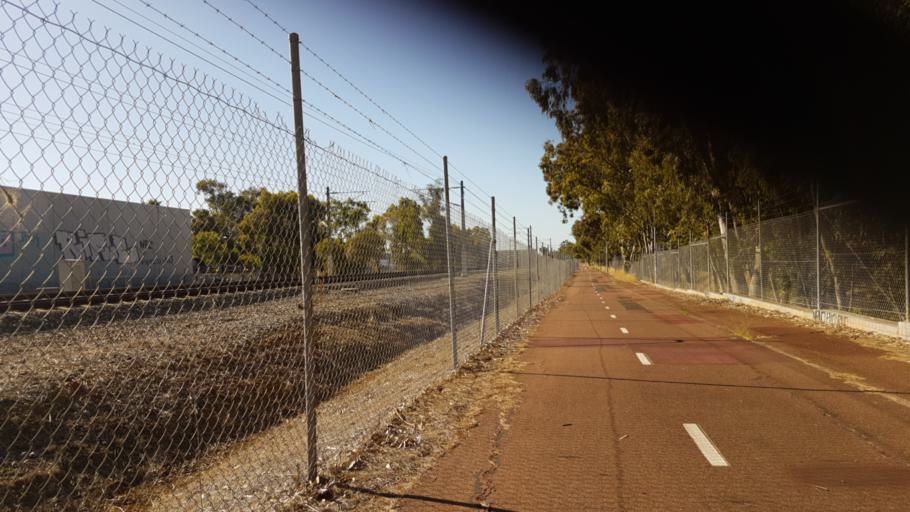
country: AU
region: Western Australia
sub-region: Gosnells
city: Maddington
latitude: -32.0427
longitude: 115.9752
